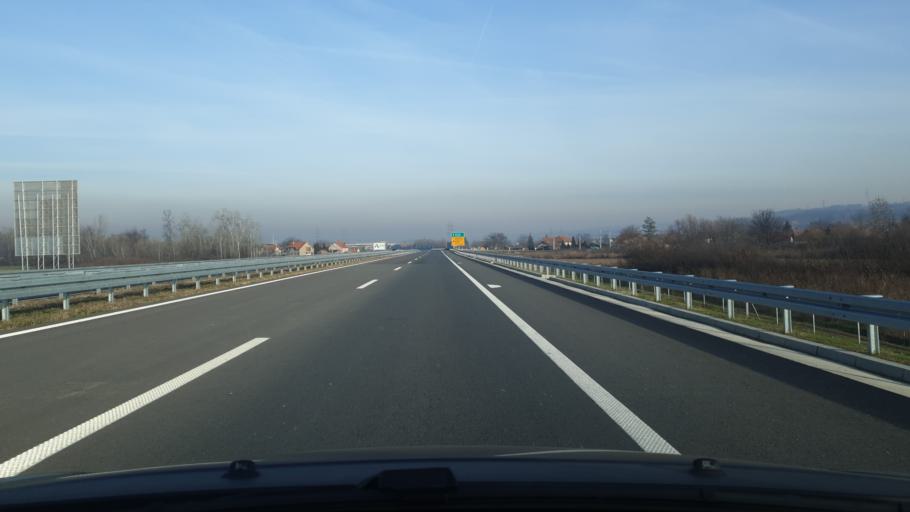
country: RS
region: Central Serbia
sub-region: Belgrade
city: Obrenovac
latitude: 44.6465
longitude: 20.2198
